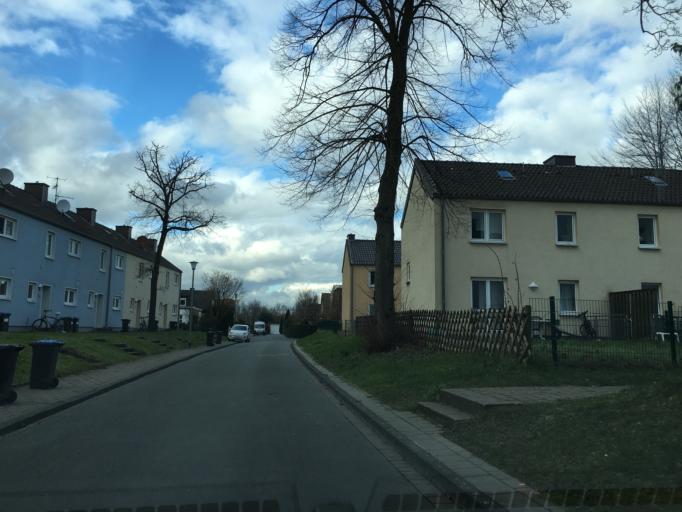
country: DE
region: North Rhine-Westphalia
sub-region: Regierungsbezirk Munster
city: Muenster
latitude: 51.9436
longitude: 7.6540
